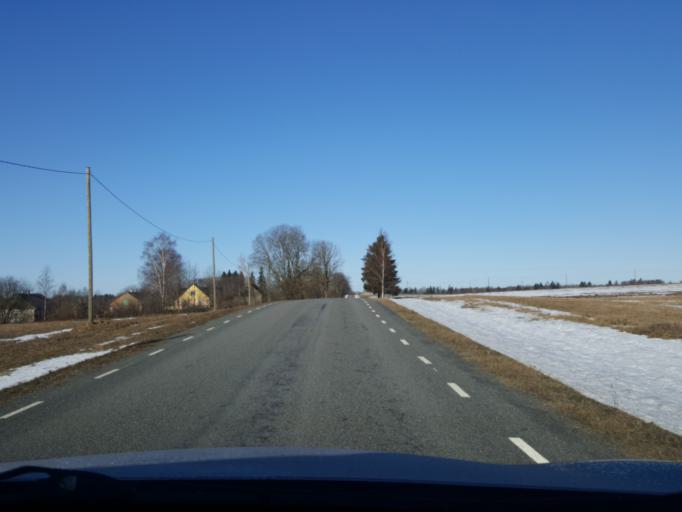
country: EE
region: Viljandimaa
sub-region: Viljandi linn
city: Viljandi
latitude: 58.4107
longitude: 25.5587
